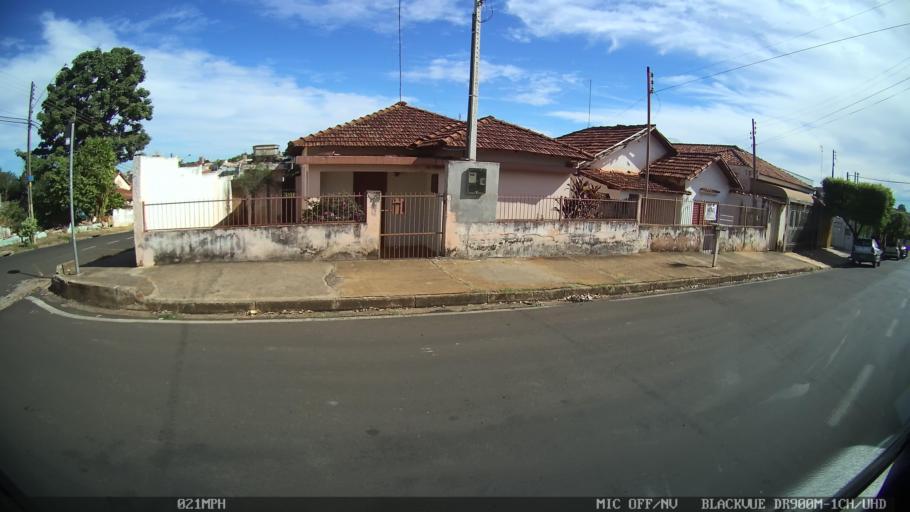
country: BR
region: Sao Paulo
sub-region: Catanduva
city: Catanduva
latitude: -21.1278
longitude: -48.9605
